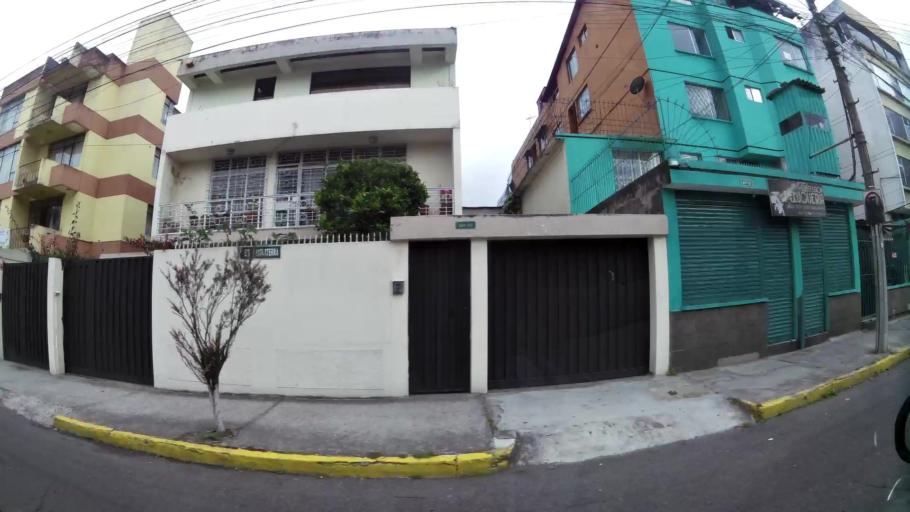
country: EC
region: Pichincha
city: Quito
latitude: -0.1902
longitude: -78.4915
